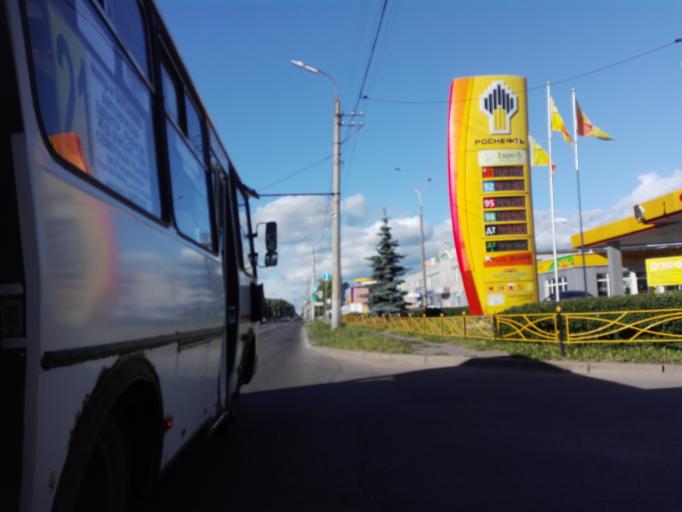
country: RU
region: Orjol
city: Orel
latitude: 53.0008
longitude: 36.1391
